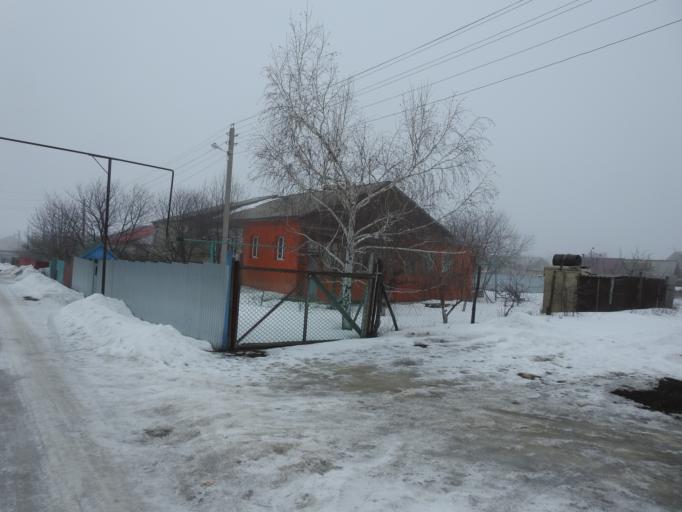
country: RU
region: Saratov
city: Sokolovyy
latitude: 51.4958
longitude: 45.8652
